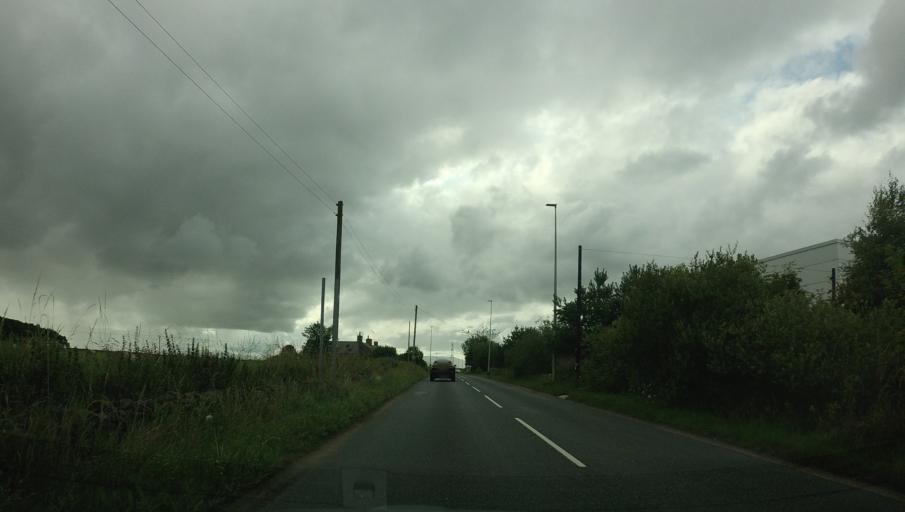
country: GB
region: Scotland
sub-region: Aberdeenshire
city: Westhill
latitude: 57.1438
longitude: -2.2955
